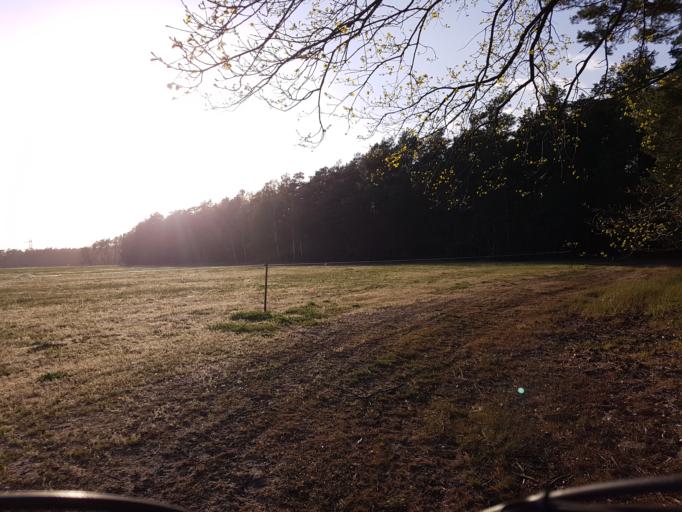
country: DE
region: Brandenburg
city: Schilda
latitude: 51.5982
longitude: 13.3825
